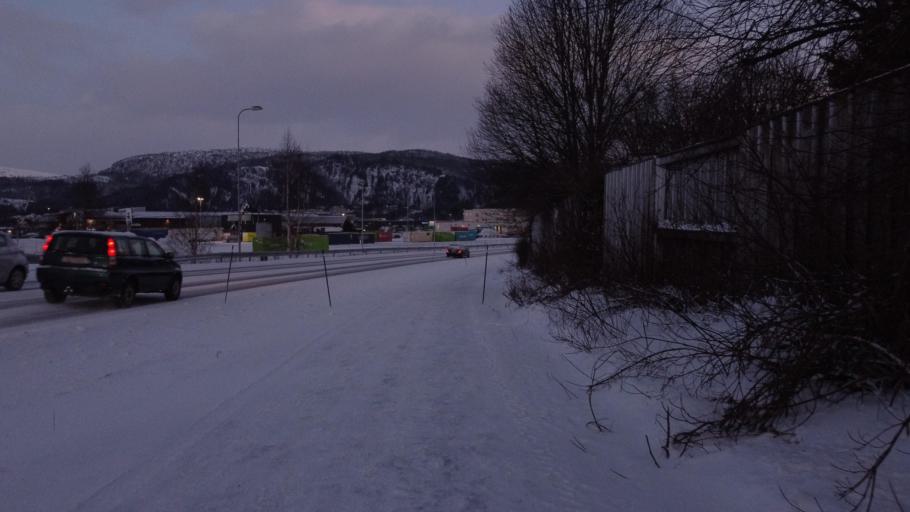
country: NO
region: Nordland
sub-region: Rana
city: Mo i Rana
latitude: 66.3172
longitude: 14.1330
